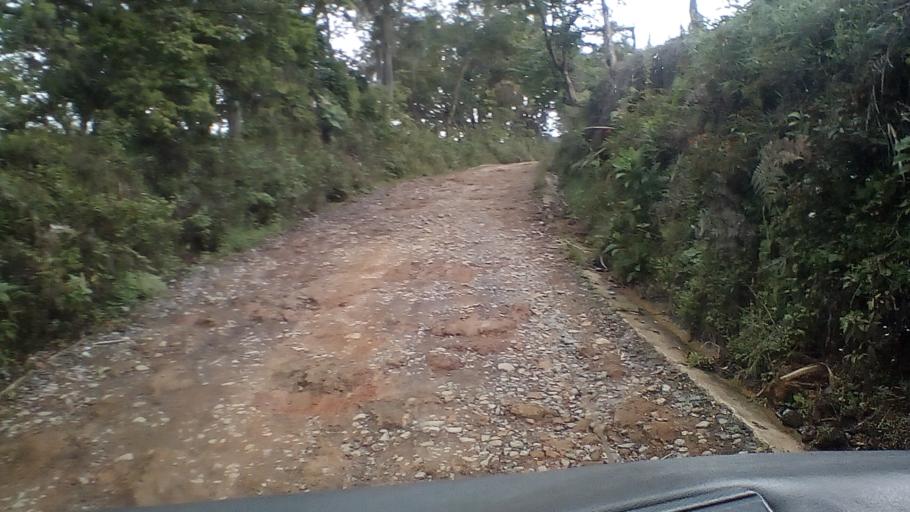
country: CO
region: Boyaca
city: Santana
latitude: 6.0146
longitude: -73.5112
